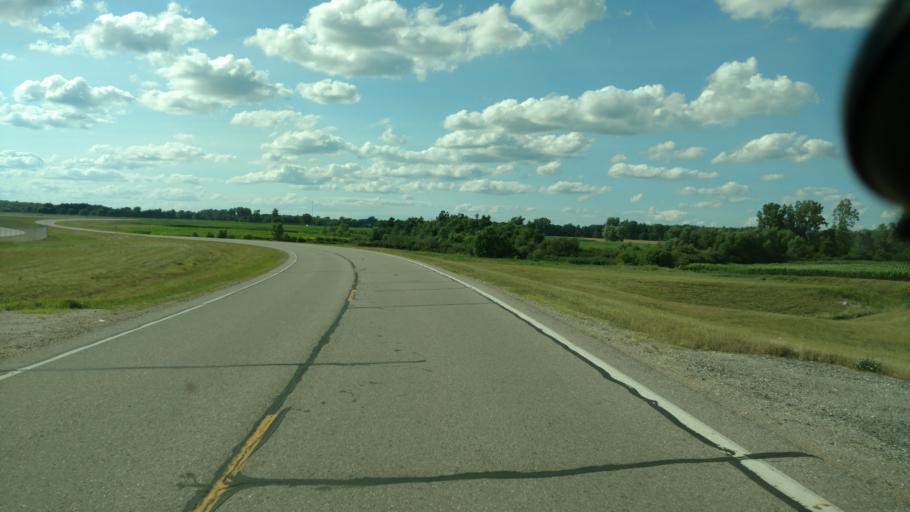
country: US
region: Michigan
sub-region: Ingham County
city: Edgemont Park
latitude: 42.7780
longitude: -84.5632
